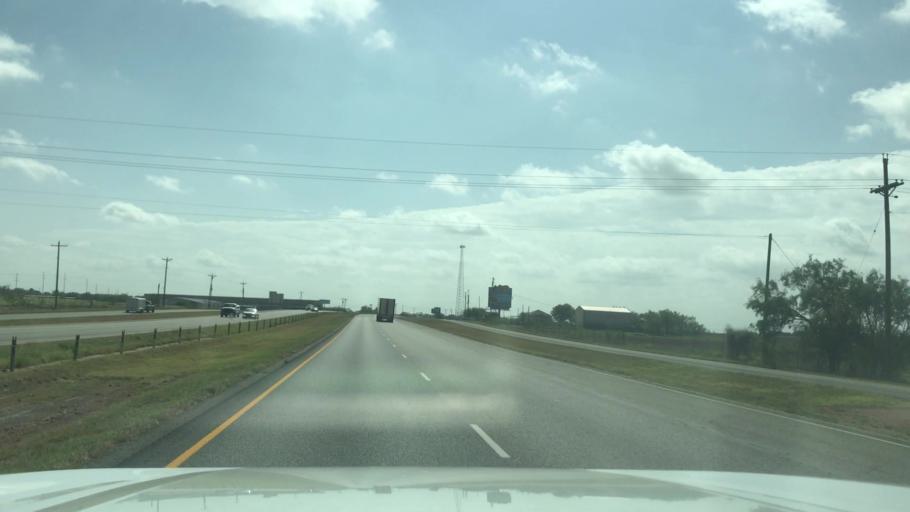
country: US
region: Texas
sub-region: Taylor County
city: Merkel
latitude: 32.4768
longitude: -100.0058
